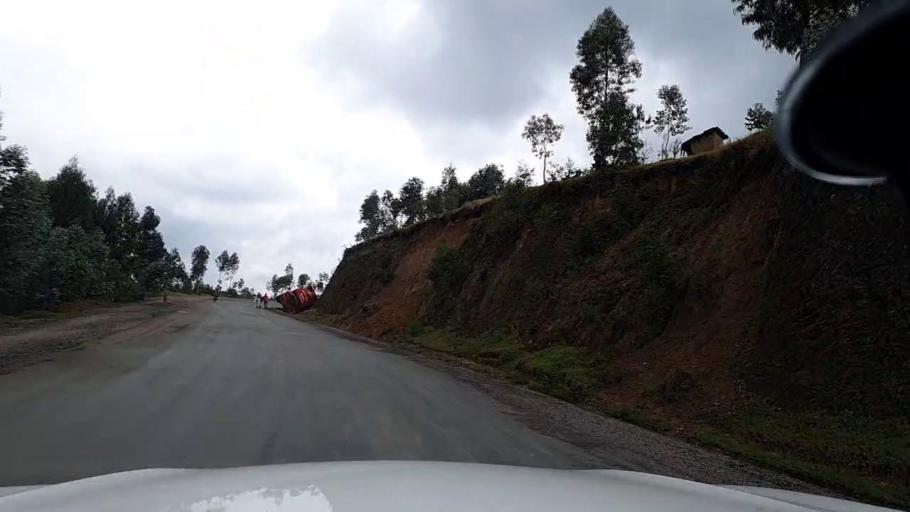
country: RW
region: Western Province
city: Kibuye
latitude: -2.0579
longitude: 29.5214
